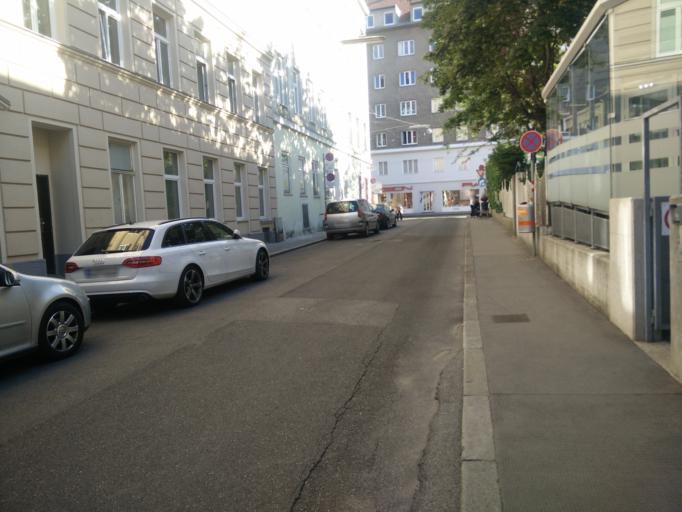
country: AT
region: Vienna
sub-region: Wien Stadt
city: Vienna
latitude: 48.2162
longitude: 16.3450
